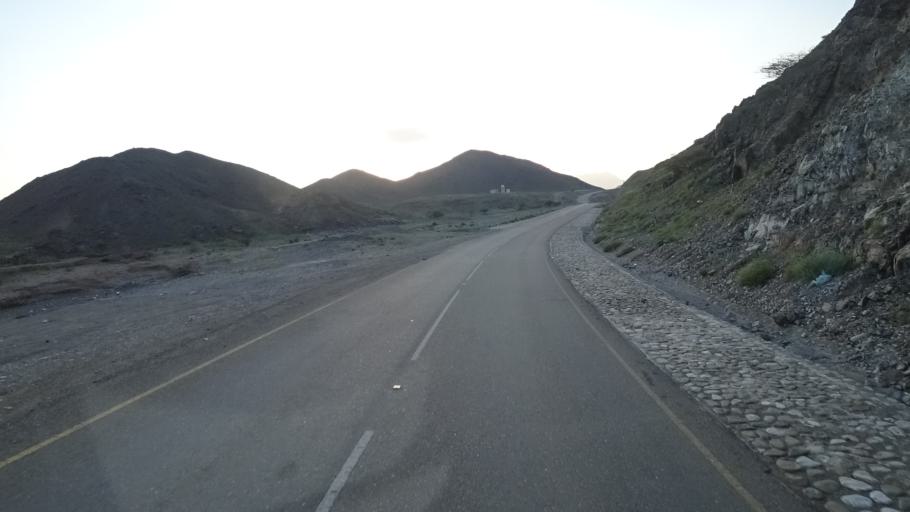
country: OM
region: Al Batinah
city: Al Khaburah
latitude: 23.7952
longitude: 56.9831
